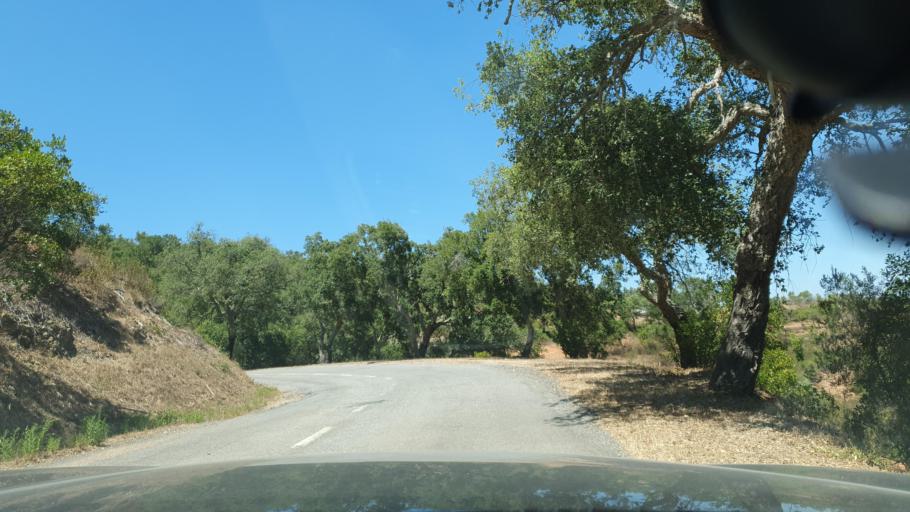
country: PT
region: Beja
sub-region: Odemira
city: Odemira
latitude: 37.6070
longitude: -8.4992
